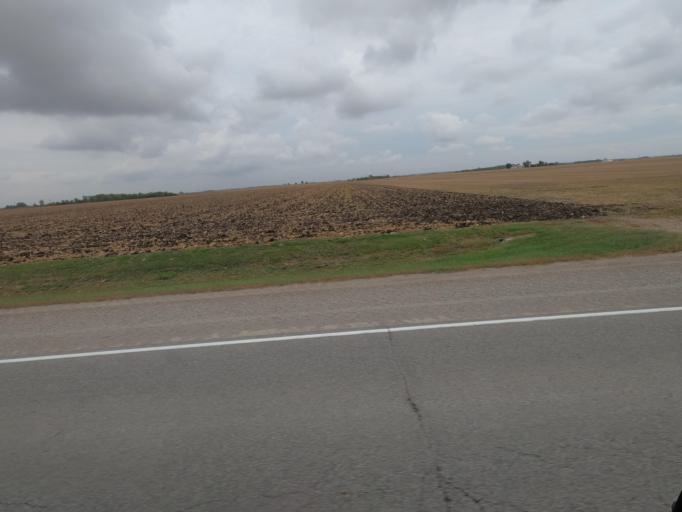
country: US
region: Iowa
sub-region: Wapello County
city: Ottumwa
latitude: 40.9840
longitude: -92.2367
